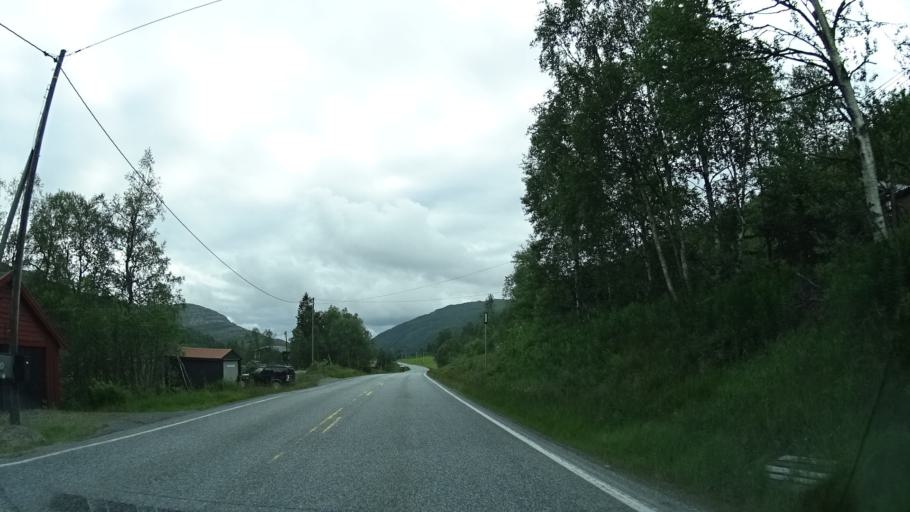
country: NO
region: Hordaland
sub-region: Samnanger
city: Tysse
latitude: 60.3939
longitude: 5.9447
